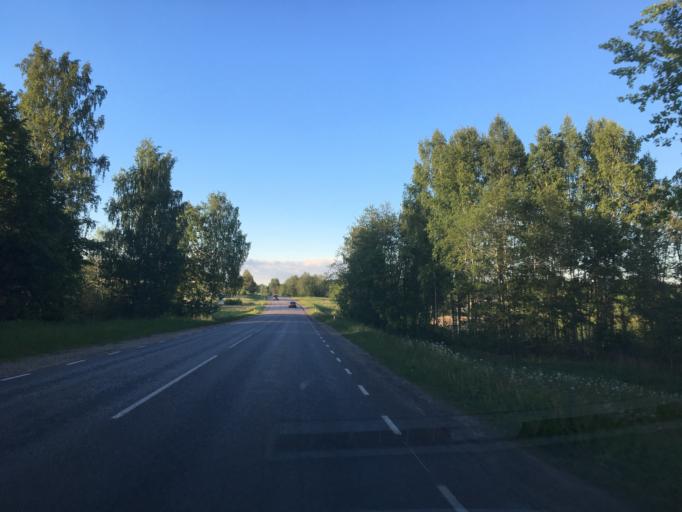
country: EE
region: Tartu
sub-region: Noo vald
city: Noo
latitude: 58.2011
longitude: 26.5728
